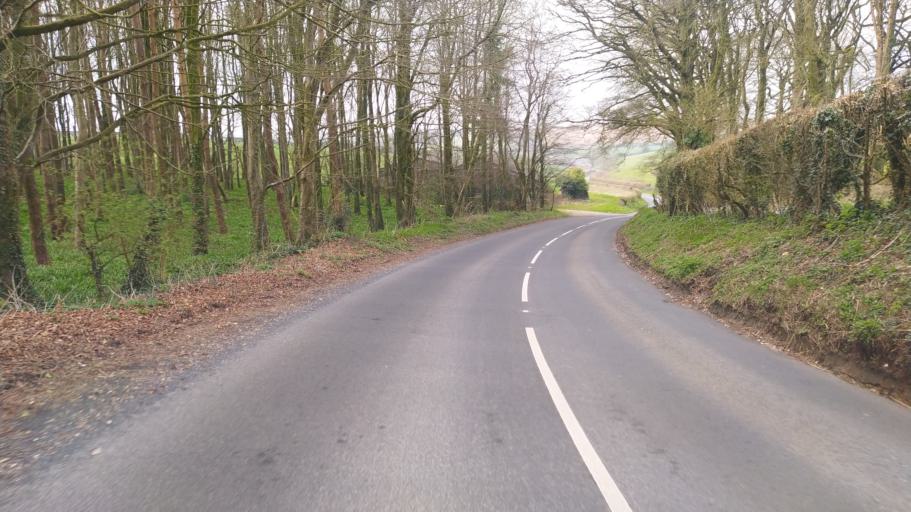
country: GB
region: England
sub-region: Dorset
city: Beaminster
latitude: 50.8206
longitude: -2.6824
